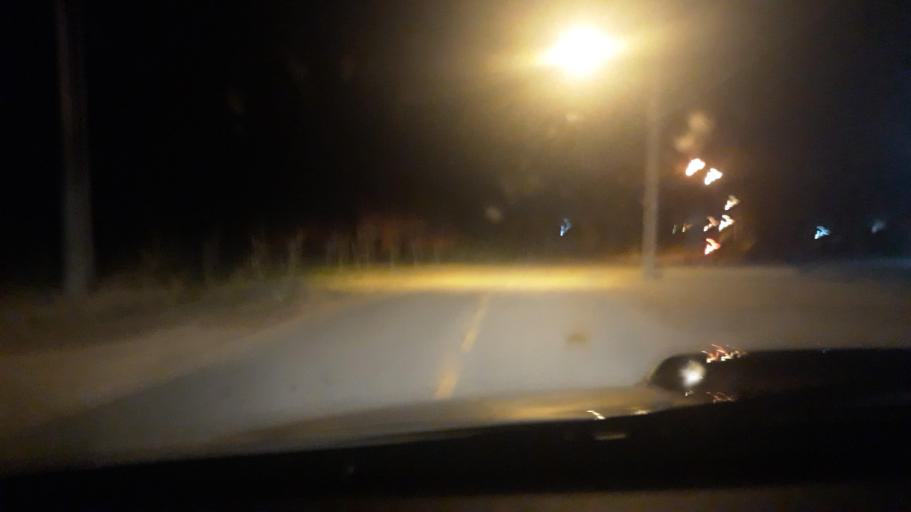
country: BR
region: Bahia
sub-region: Guanambi
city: Guanambi
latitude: -14.2862
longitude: -42.7088
